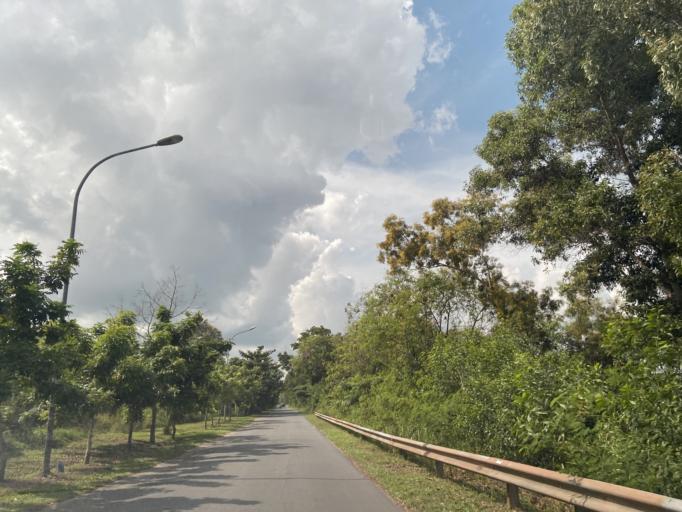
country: SG
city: Singapore
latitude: 1.1107
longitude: 104.0281
